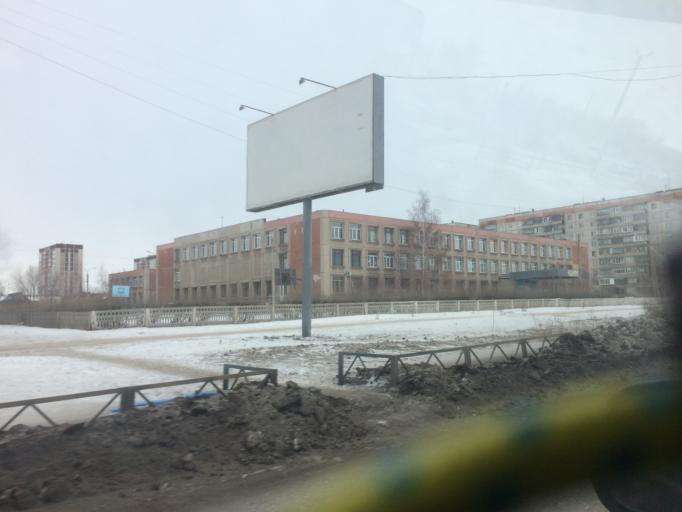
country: RU
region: Chelyabinsk
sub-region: Gorod Magnitogorsk
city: Magnitogorsk
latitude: 53.3610
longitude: 58.9848
